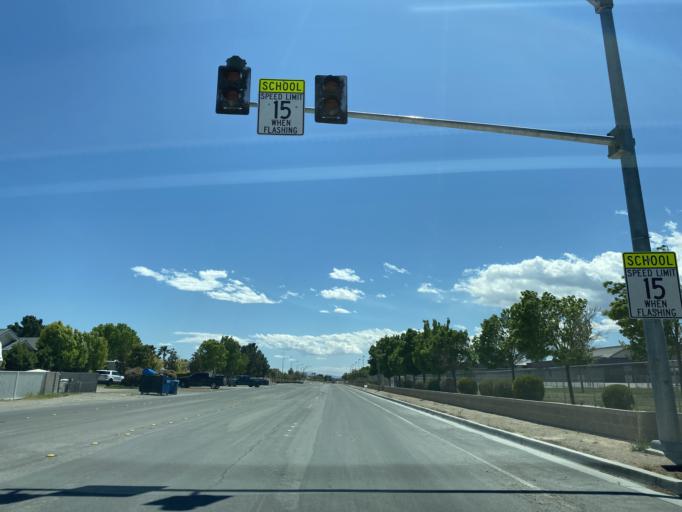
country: US
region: Nevada
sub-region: Clark County
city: North Las Vegas
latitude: 36.3087
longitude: -115.2333
